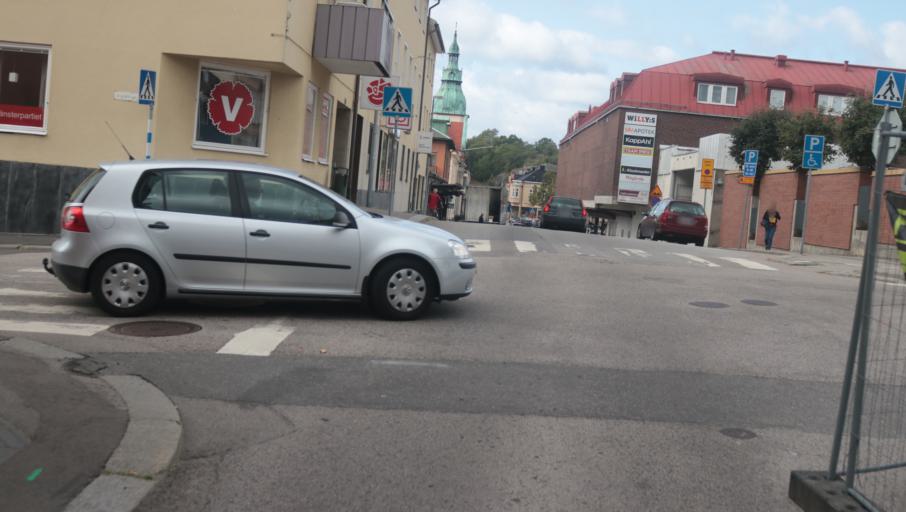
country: SE
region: Blekinge
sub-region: Karlshamns Kommun
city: Karlshamn
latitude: 56.1706
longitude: 14.8668
